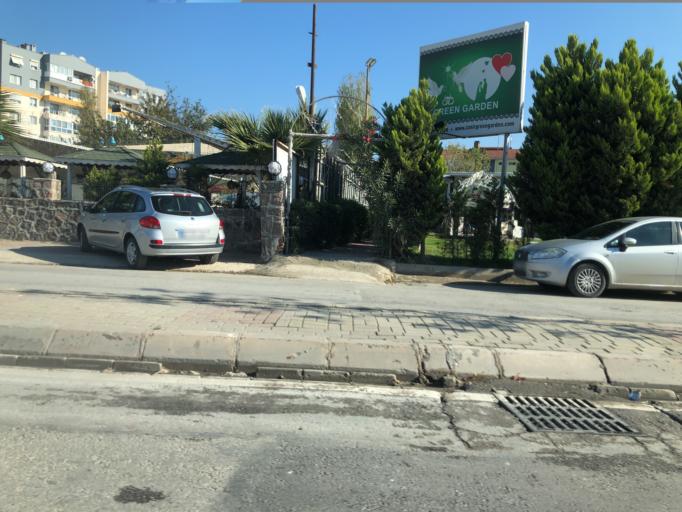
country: TR
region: Izmir
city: Izmir
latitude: 38.4567
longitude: 27.1761
